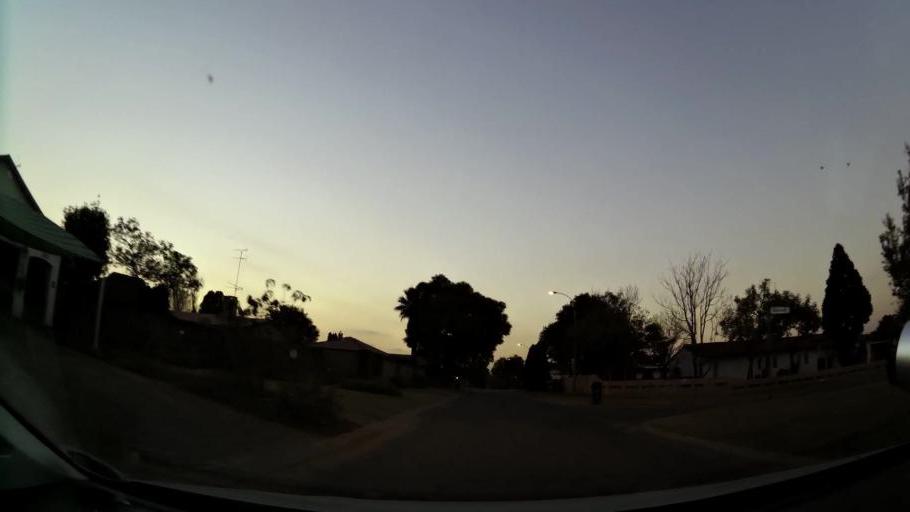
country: ZA
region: Gauteng
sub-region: Ekurhuleni Metropolitan Municipality
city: Tembisa
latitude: -26.0507
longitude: 28.2450
